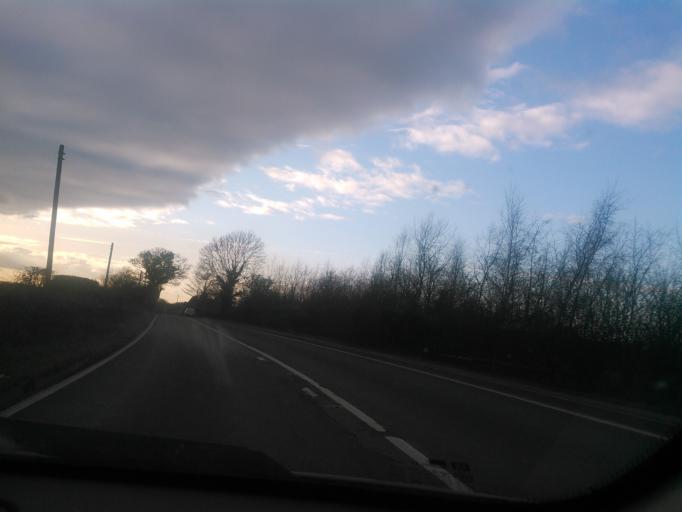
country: GB
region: England
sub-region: Shropshire
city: Stoke upon Tern
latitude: 52.8670
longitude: -2.5021
